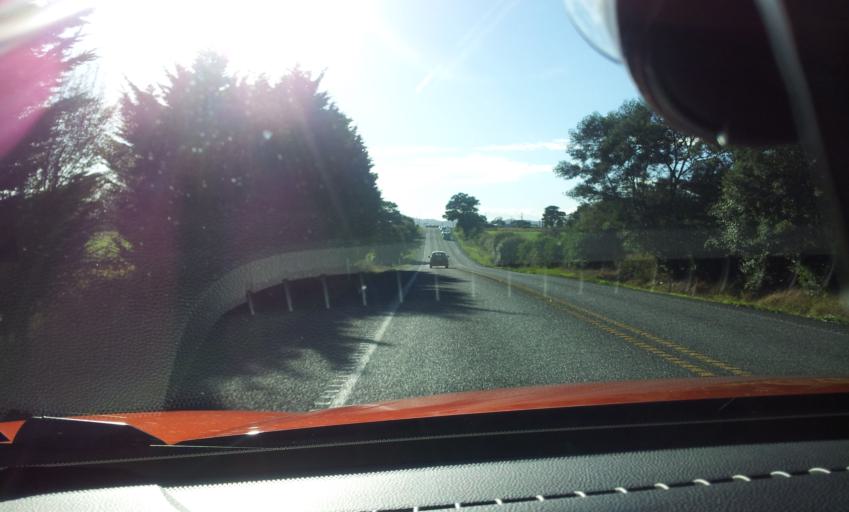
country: NZ
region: Waikato
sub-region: Waikato District
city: Te Kauwhata
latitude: -37.2460
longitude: 175.1980
